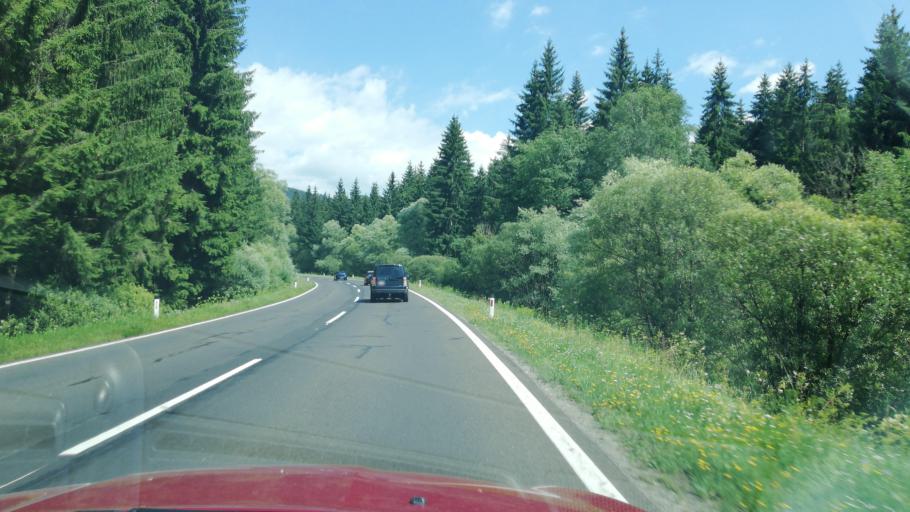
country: AT
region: Styria
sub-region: Politischer Bezirk Murau
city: Sankt Marein bei Neumarkt
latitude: 47.0254
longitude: 14.4179
